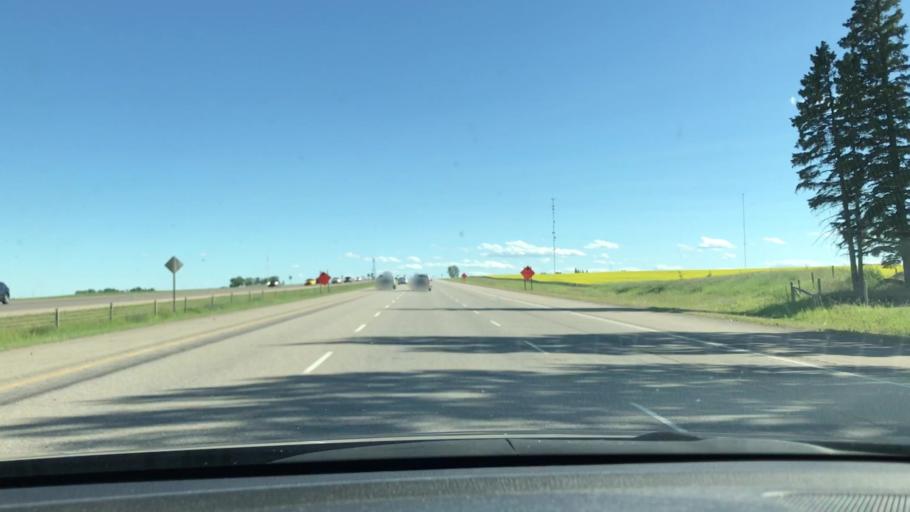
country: CA
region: Alberta
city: Crossfield
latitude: 51.4303
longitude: -114.0020
